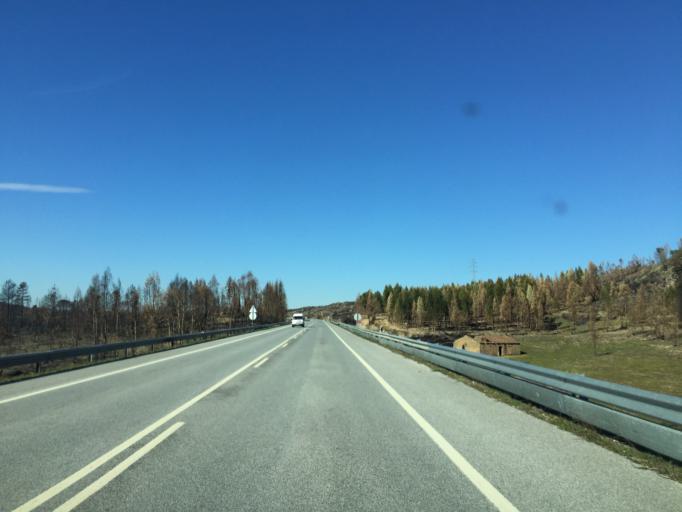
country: PT
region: Portalegre
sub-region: Nisa
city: Nisa
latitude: 39.5196
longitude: -7.7726
